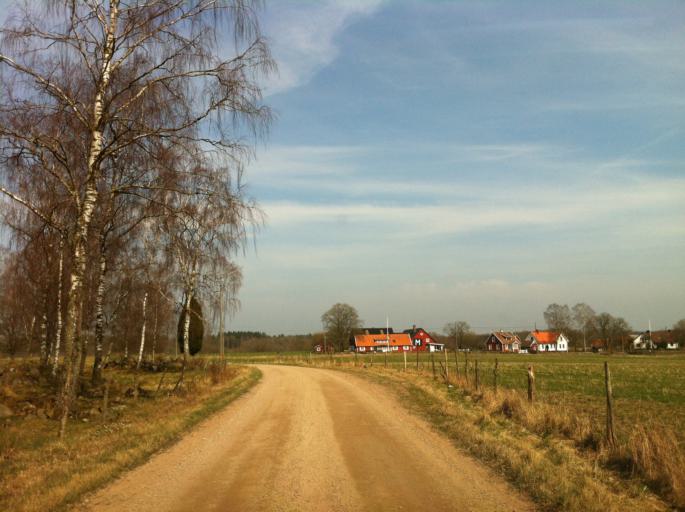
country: SE
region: Skane
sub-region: Eslovs Kommun
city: Stehag
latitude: 56.0148
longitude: 13.3550
